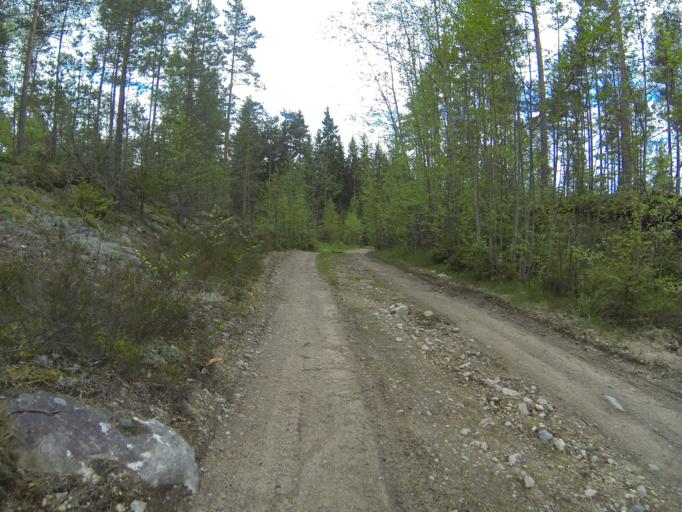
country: FI
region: Varsinais-Suomi
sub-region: Salo
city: Halikko
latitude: 60.3353
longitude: 23.0786
